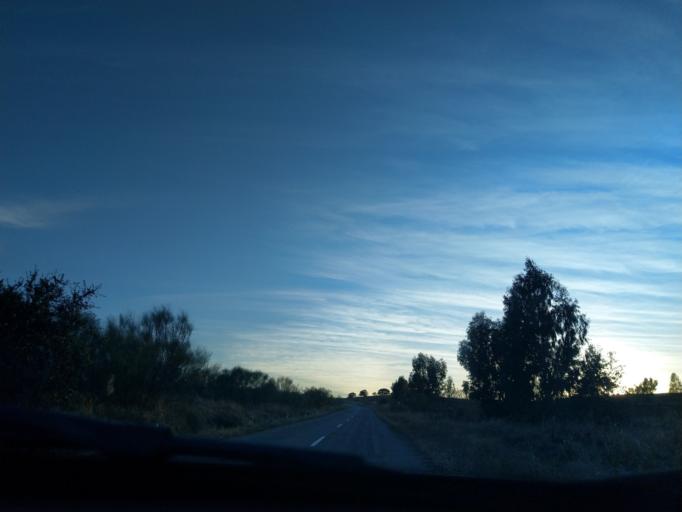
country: ES
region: Extremadura
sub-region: Provincia de Badajoz
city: Valverde de Llerena
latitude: 38.1984
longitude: -5.8498
